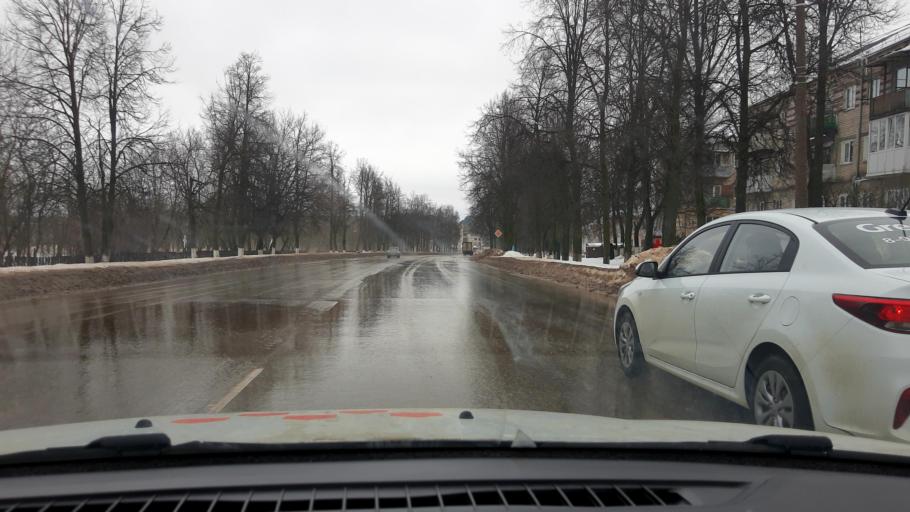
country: RU
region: Nizjnij Novgorod
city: Pavlovo
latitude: 55.9655
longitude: 43.1090
